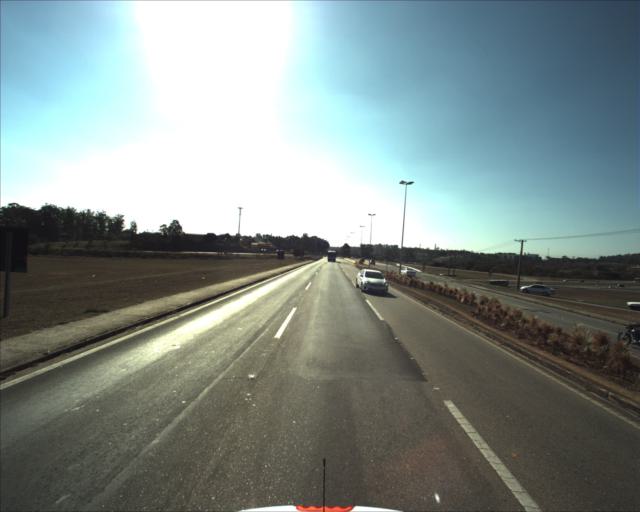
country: BR
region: Sao Paulo
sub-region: Sorocaba
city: Sorocaba
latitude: -23.4706
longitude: -47.4236
